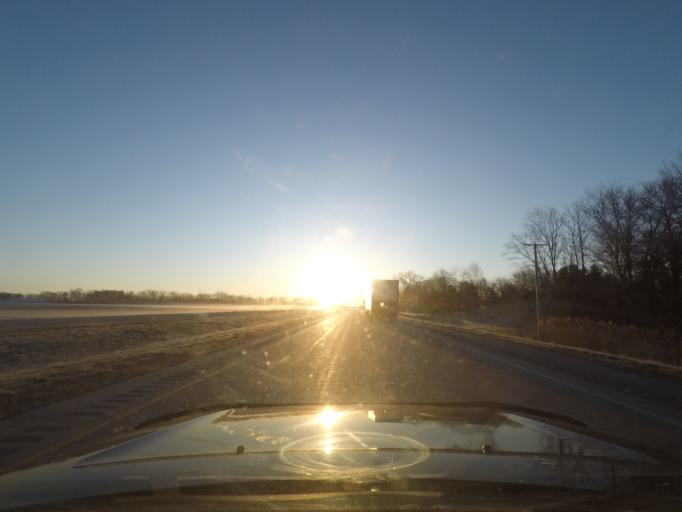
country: US
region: Indiana
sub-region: Marshall County
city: Plymouth
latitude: 41.4496
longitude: -86.3026
